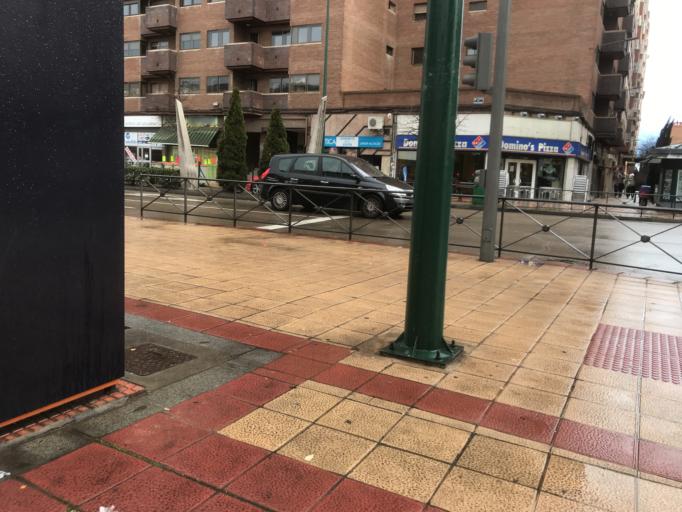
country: ES
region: Castille and Leon
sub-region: Provincia de Valladolid
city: Valladolid
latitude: 41.6411
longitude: -4.7345
